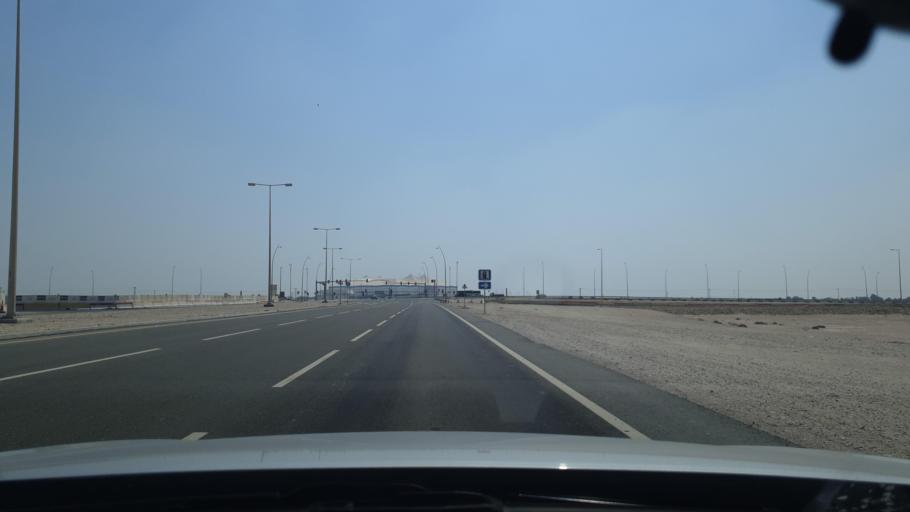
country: QA
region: Al Khawr
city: Al Khawr
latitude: 25.6674
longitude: 51.4740
